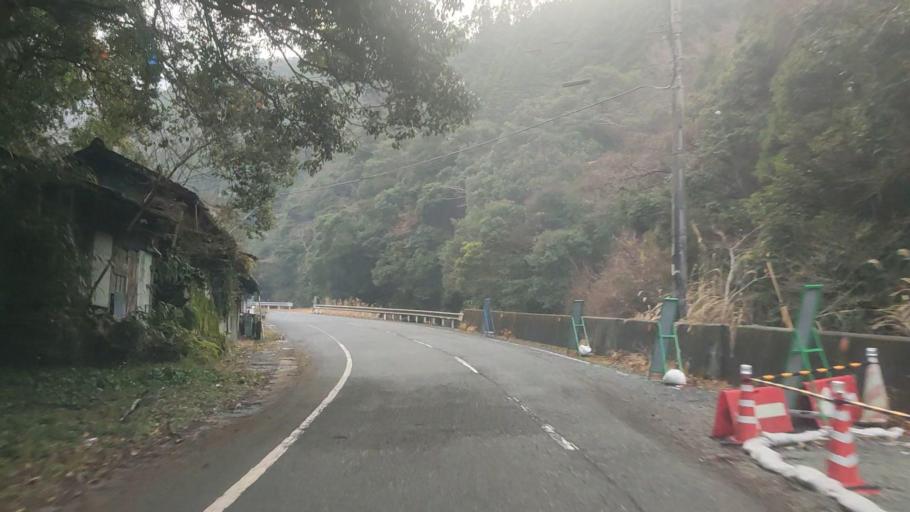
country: JP
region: Kumamoto
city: Matsubase
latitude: 32.6027
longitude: 130.8869
